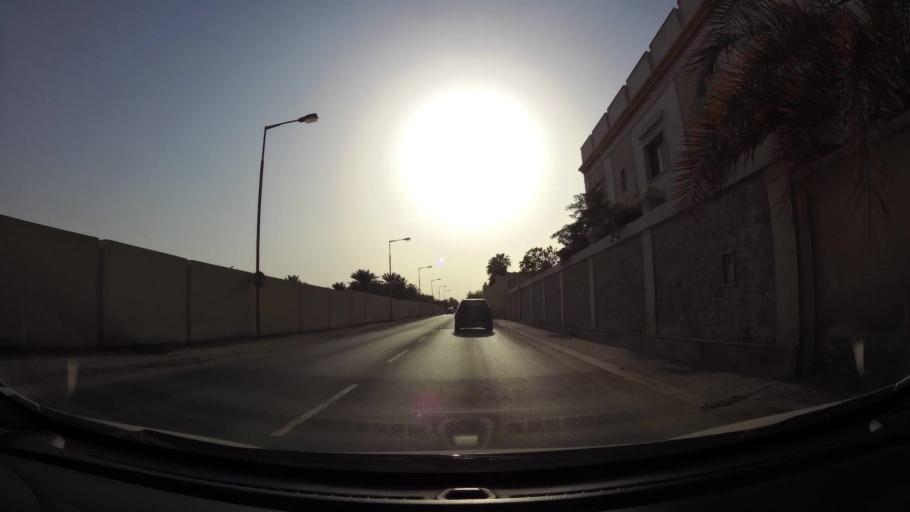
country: BH
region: Manama
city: Jidd Hafs
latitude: 26.2033
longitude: 50.4885
